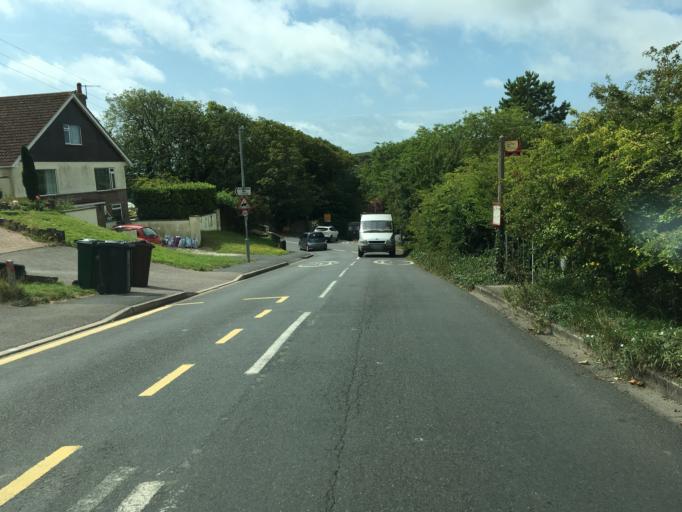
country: GB
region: England
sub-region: Brighton and Hove
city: Rottingdean
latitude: 50.8195
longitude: -0.0742
